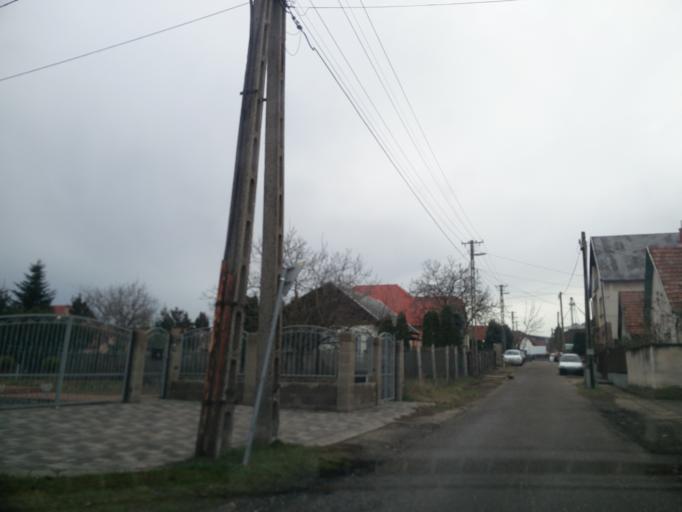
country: HU
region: Pest
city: Orbottyan
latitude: 47.6561
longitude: 19.2340
